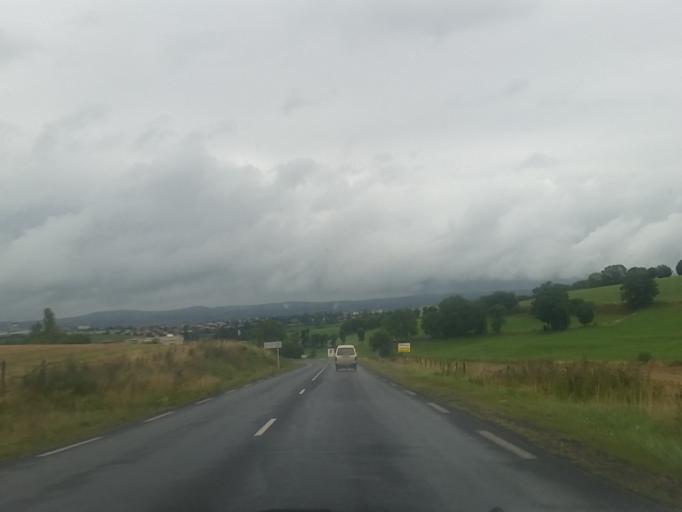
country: FR
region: Auvergne
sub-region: Departement du Cantal
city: Saint-Flour
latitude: 45.0219
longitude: 3.0618
